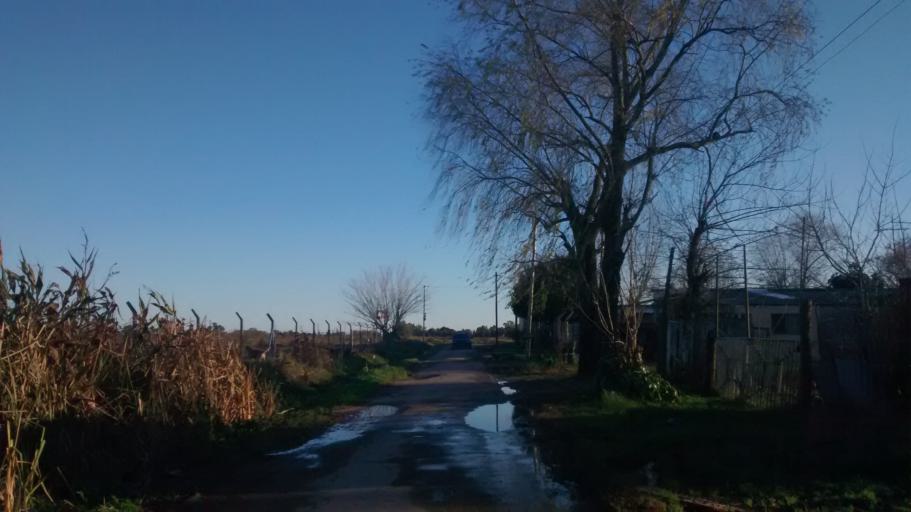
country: AR
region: Buenos Aires
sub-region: Partido de La Plata
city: La Plata
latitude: -34.9645
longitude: -57.9361
